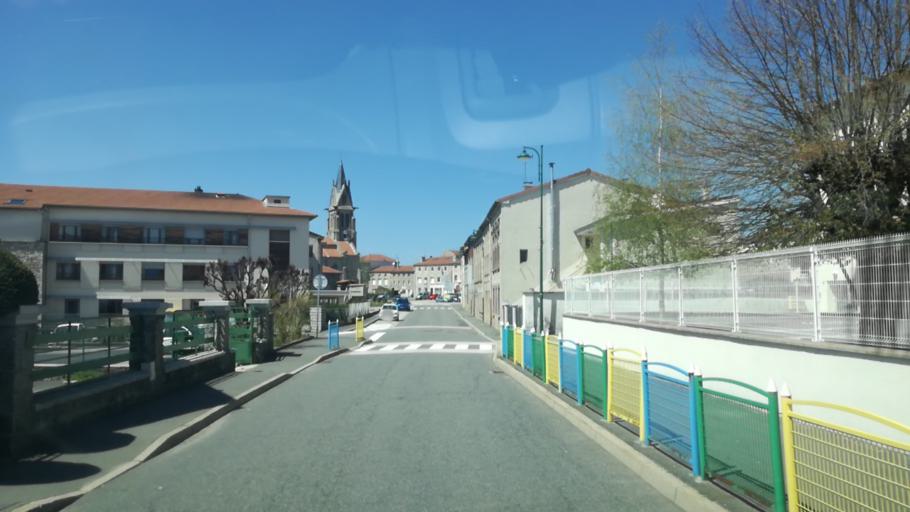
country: FR
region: Rhone-Alpes
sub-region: Departement de la Loire
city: Jonzieux
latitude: 45.3134
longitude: 4.3623
